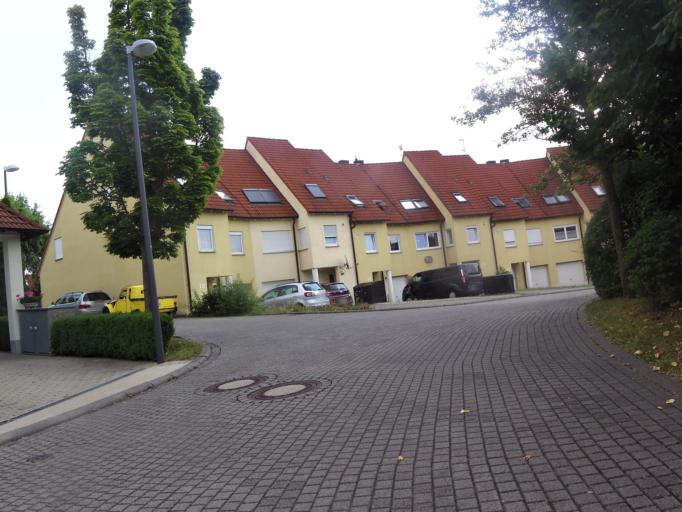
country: DE
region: Bavaria
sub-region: Regierungsbezirk Unterfranken
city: Randersacker
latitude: 49.7365
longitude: 9.9592
